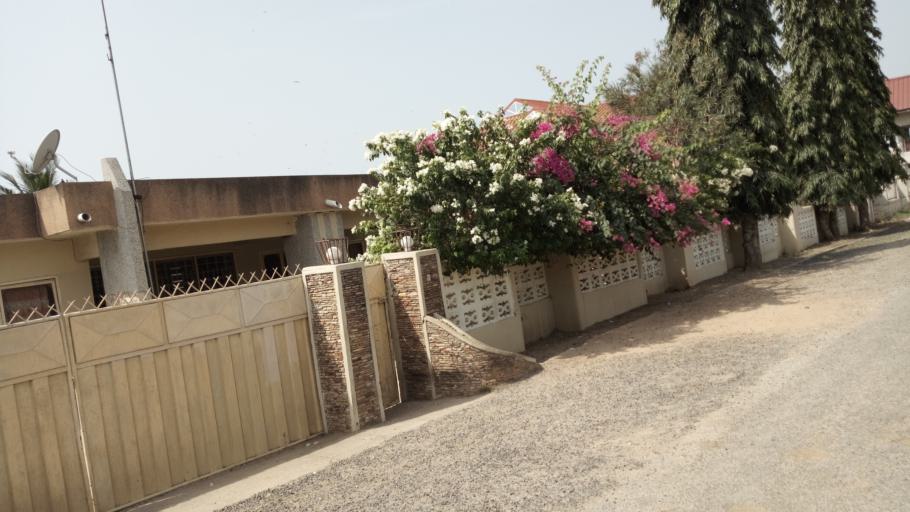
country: GH
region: Central
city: Winneba
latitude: 5.3685
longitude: -0.6412
